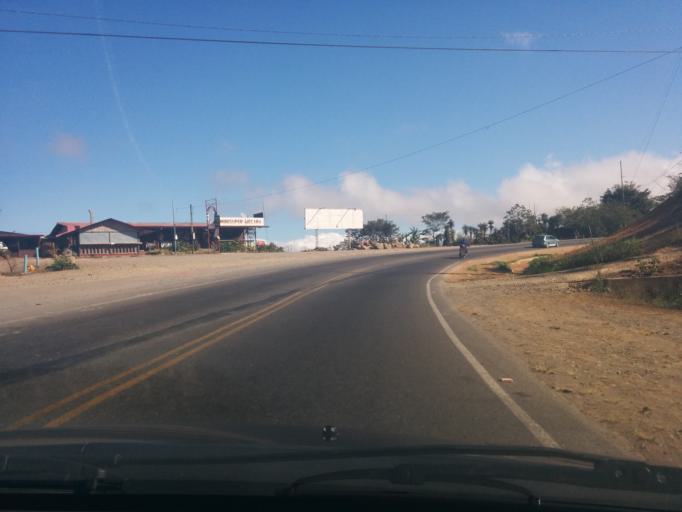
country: CR
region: Alajuela
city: San Rafael
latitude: 10.0492
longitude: -84.5071
